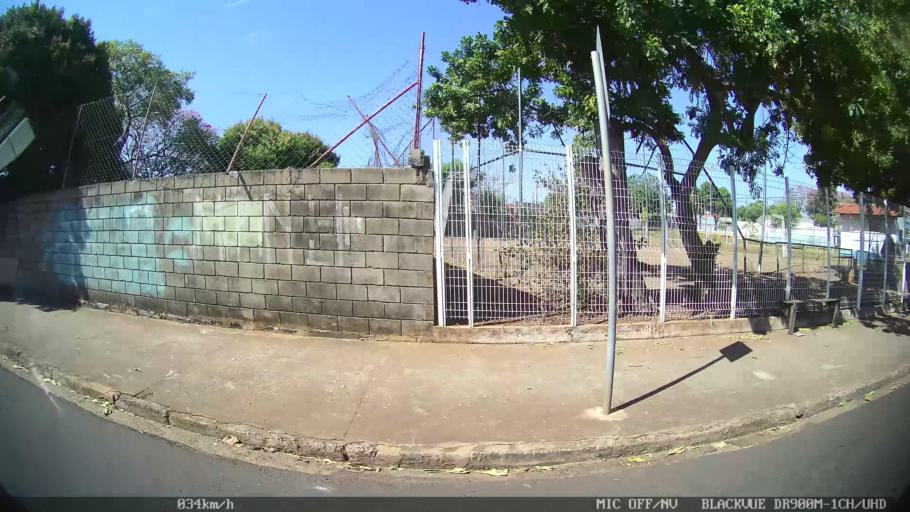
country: BR
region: Sao Paulo
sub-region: Sao Jose Do Rio Preto
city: Sao Jose do Rio Preto
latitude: -20.7749
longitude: -49.4183
